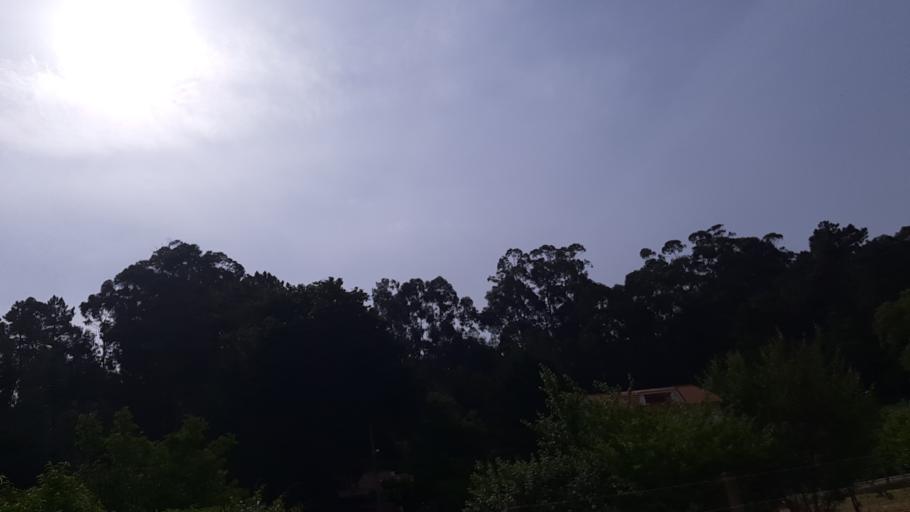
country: ES
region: Galicia
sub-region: Provincia de Pontevedra
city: O Rosal
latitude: 41.9183
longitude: -8.8273
